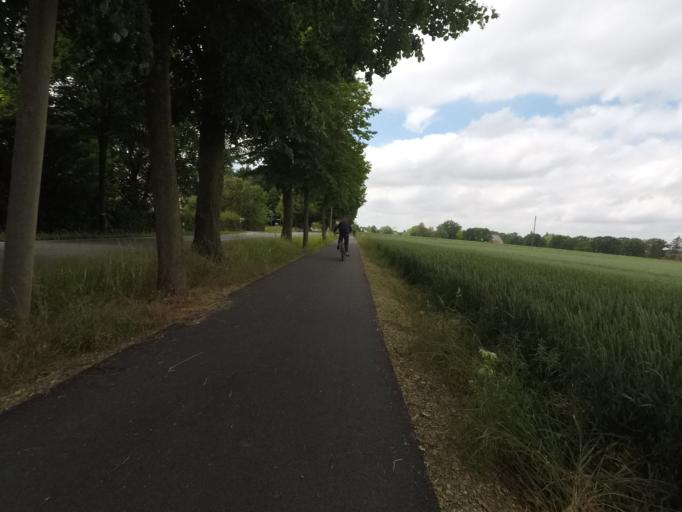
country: DE
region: North Rhine-Westphalia
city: Enger
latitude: 52.1320
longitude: 8.5236
